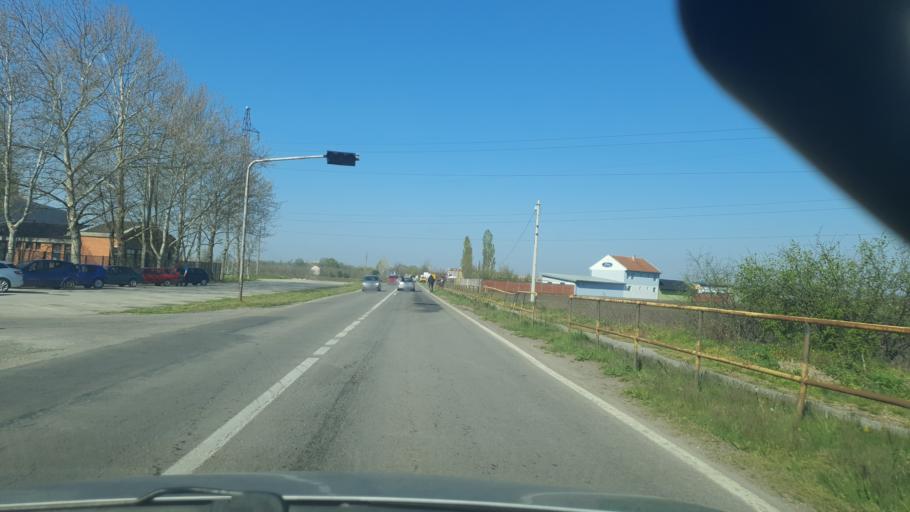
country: RS
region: Autonomna Pokrajina Vojvodina
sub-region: Zapadnobacki Okrug
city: Sombor
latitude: 45.7683
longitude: 19.1484
